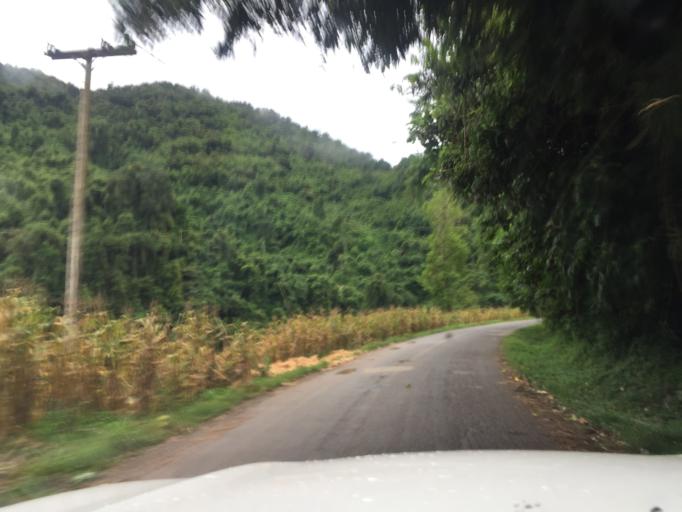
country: LA
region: Oudomxai
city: Muang La
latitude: 20.9510
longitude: 102.2143
